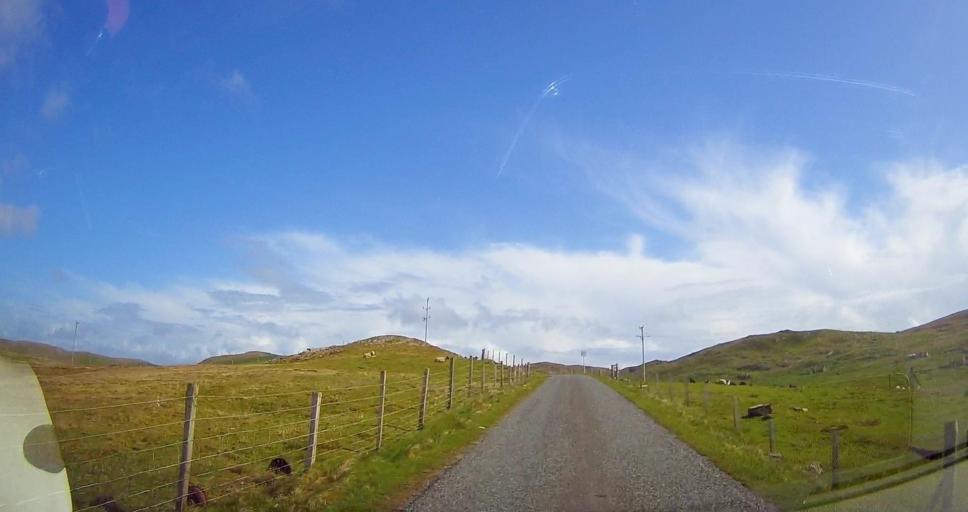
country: GB
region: Scotland
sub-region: Shetland Islands
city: Lerwick
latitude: 60.5932
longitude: -1.3294
